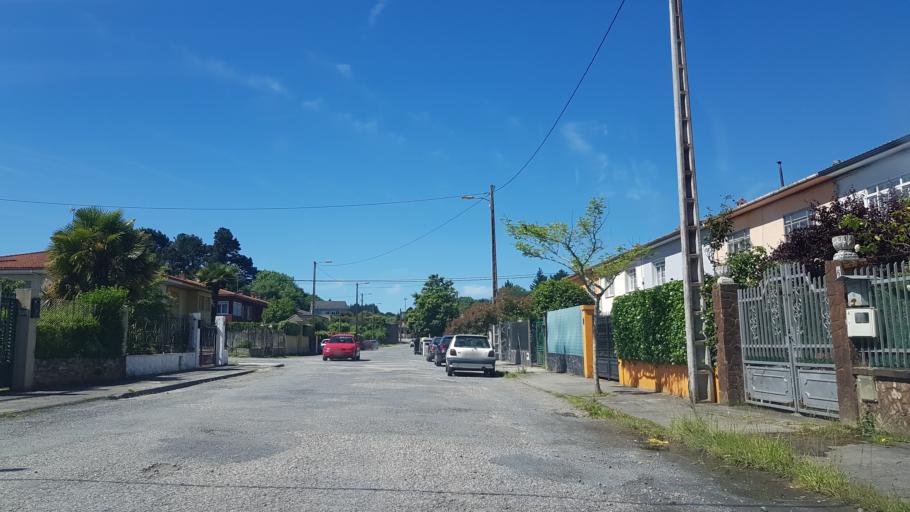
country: ES
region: Galicia
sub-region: Provincia de Lugo
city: Lugo
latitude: 43.0278
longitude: -7.5415
